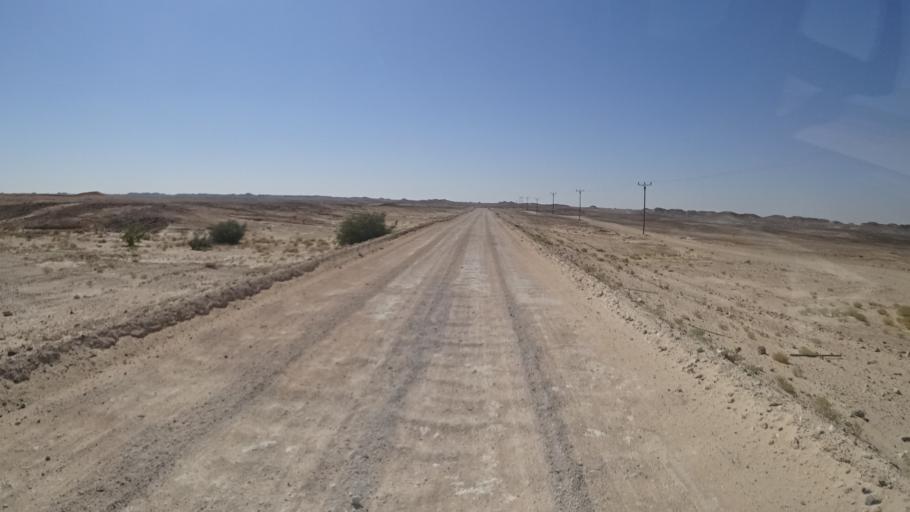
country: YE
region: Al Mahrah
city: Hawf
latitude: 17.3754
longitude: 53.2038
